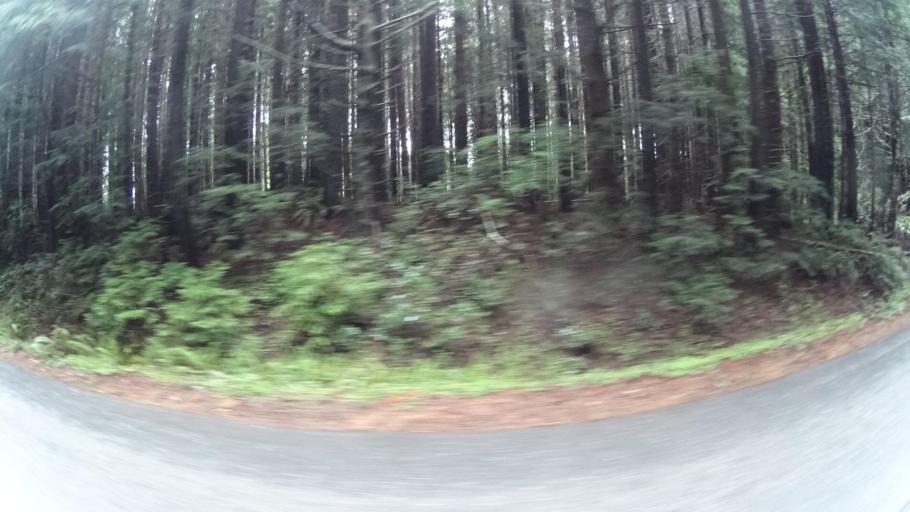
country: US
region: California
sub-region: Humboldt County
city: Westhaven-Moonstone
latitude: 41.2361
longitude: -123.9808
